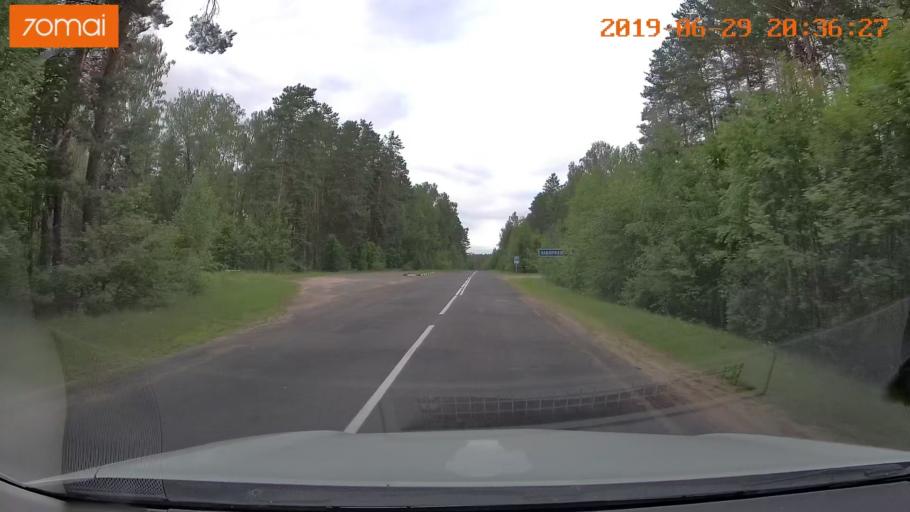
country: BY
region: Brest
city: Hantsavichy
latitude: 52.5264
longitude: 26.3586
